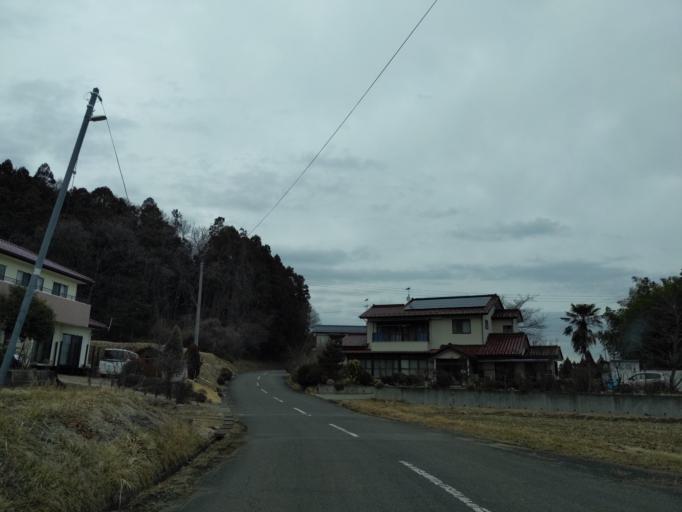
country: JP
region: Fukushima
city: Motomiya
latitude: 37.4698
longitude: 140.3975
